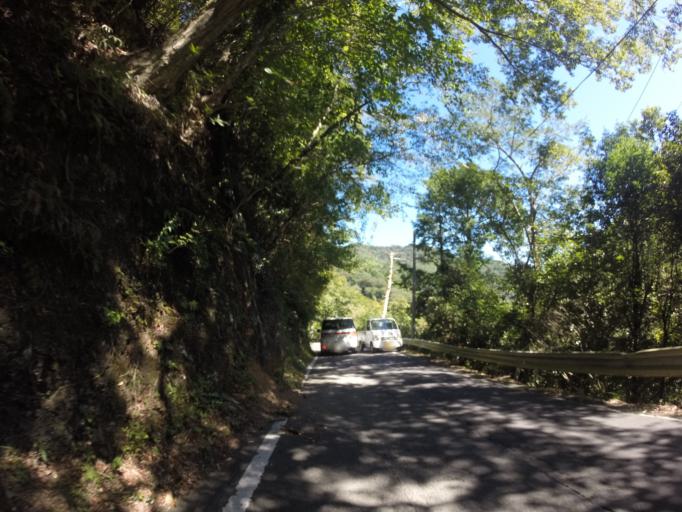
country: JP
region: Shizuoka
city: Kanaya
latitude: 34.9068
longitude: 138.1203
